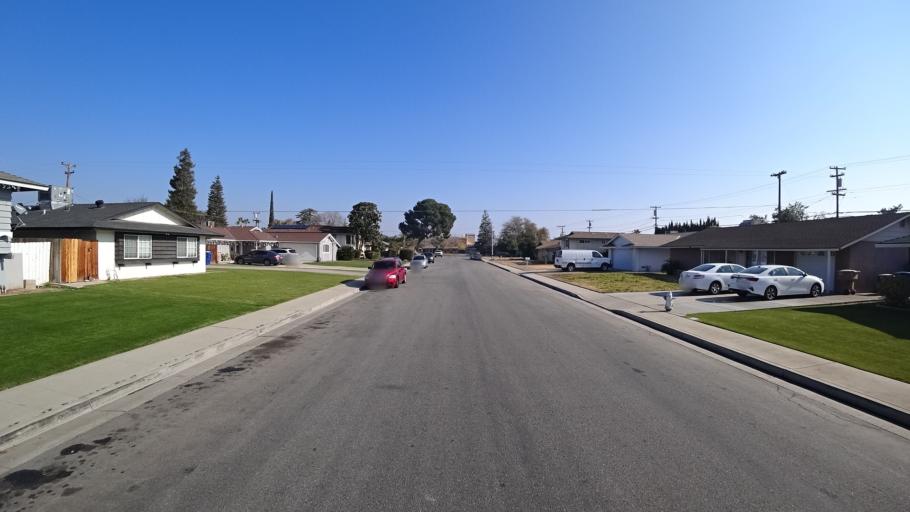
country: US
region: California
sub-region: Kern County
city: Greenacres
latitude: 35.3553
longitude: -119.0676
